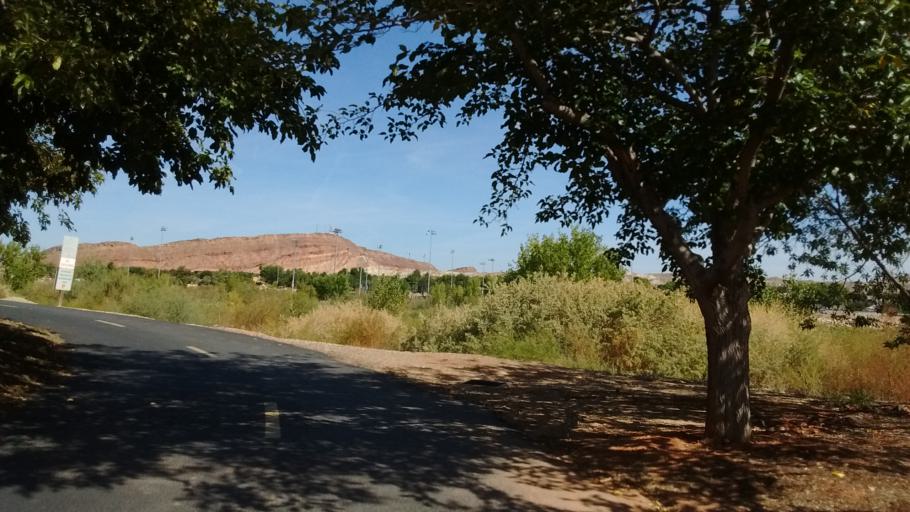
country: US
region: Utah
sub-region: Washington County
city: Saint George
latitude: 37.0526
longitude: -113.6021
